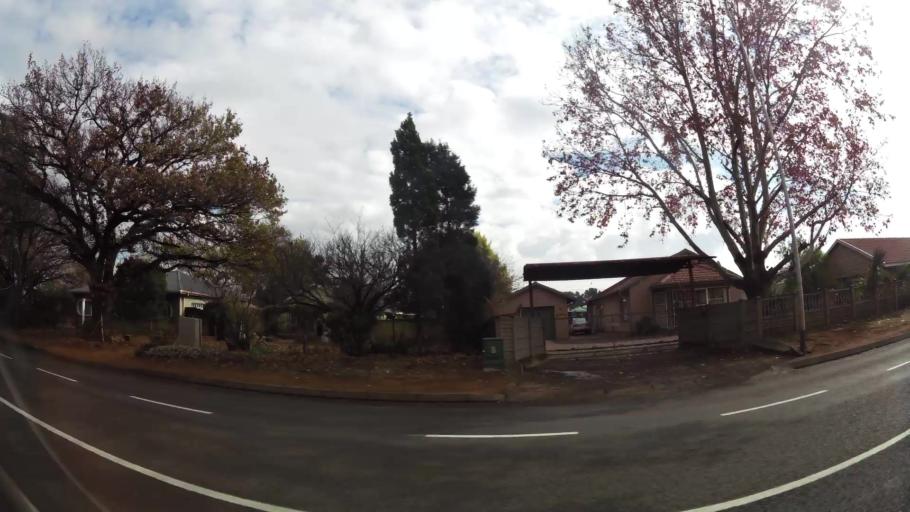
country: ZA
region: Gauteng
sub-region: Sedibeng District Municipality
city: Meyerton
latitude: -26.5911
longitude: 27.9994
